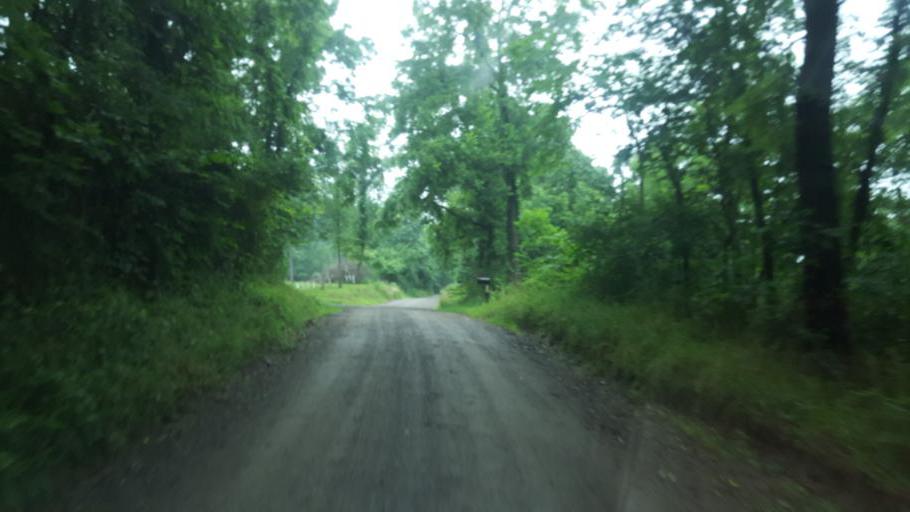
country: US
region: Ohio
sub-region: Columbiana County
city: Salineville
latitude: 40.5322
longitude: -80.8291
